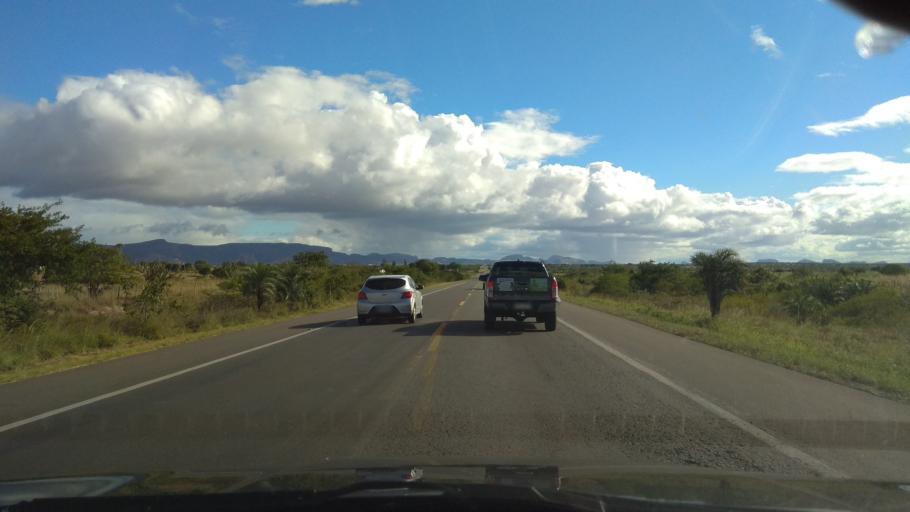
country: BR
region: Bahia
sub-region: Castro Alves
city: Castro Alves
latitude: -12.6664
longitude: -39.6417
